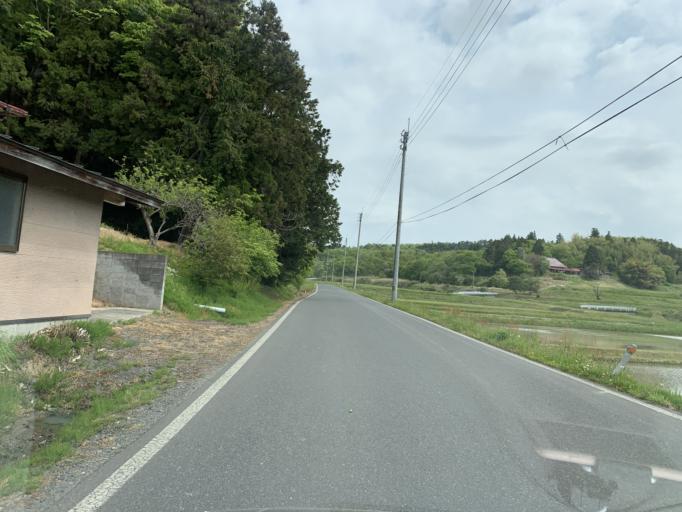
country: JP
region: Iwate
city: Ichinoseki
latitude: 38.8450
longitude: 141.1950
